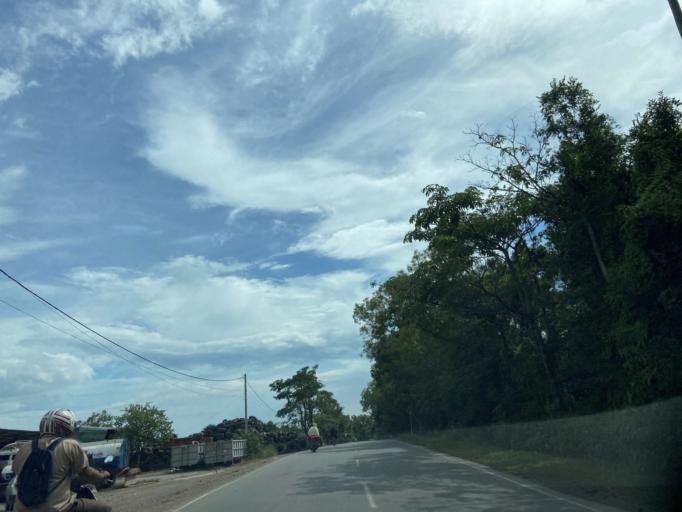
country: SG
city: Singapore
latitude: 1.0537
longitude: 103.9565
